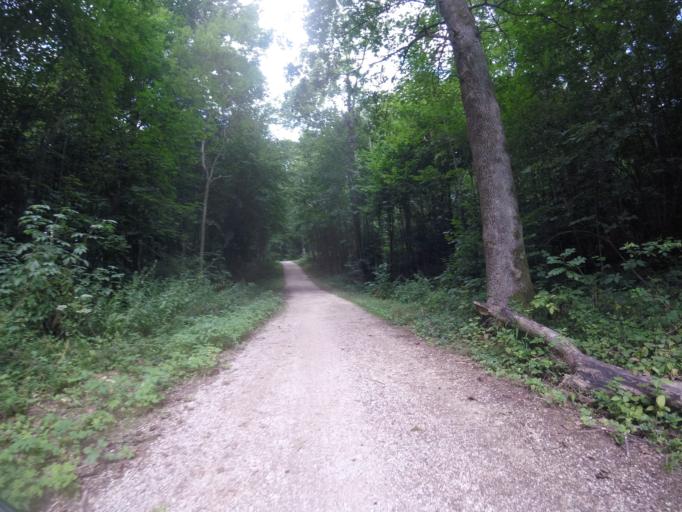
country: DE
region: Baden-Wuerttemberg
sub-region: Regierungsbezirk Stuttgart
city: Mutlangen
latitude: 48.8165
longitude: 9.7929
